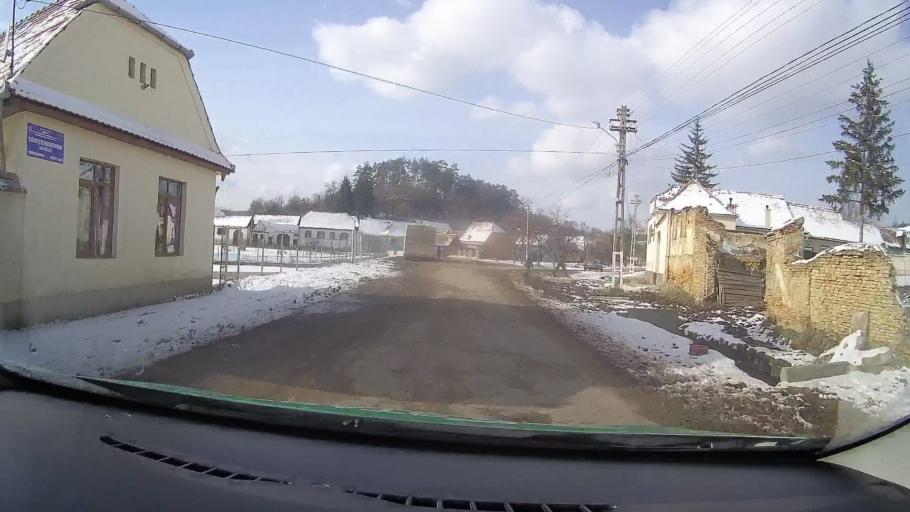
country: RO
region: Sibiu
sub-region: Comuna Iacobeni
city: Iacobeni
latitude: 46.0521
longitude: 24.7152
